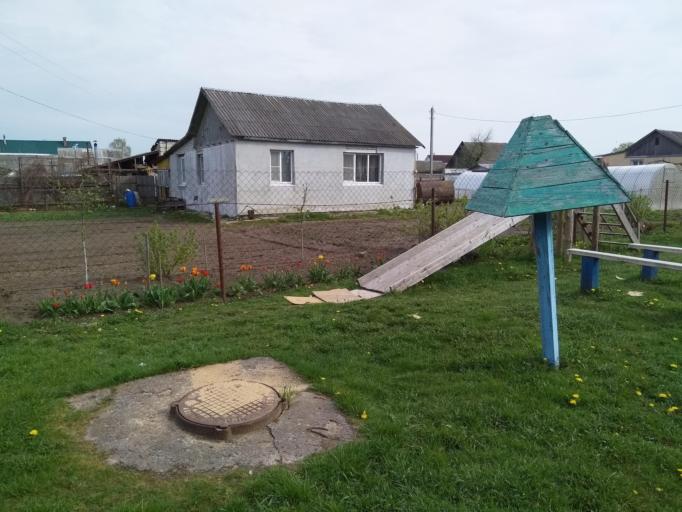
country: BY
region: Mogilev
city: Dashkawka
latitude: 53.7312
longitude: 30.2592
